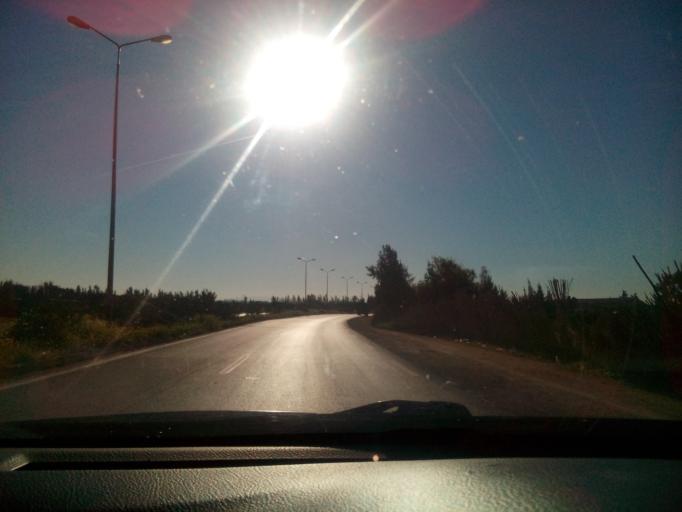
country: DZ
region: Relizane
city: Relizane
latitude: 35.7486
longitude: 0.6131
